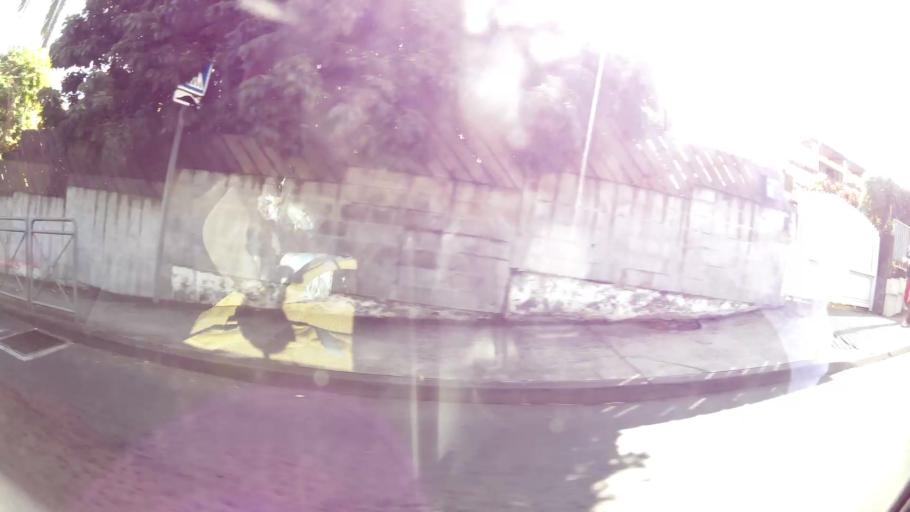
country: RE
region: Reunion
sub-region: Reunion
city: Le Tampon
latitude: -21.2811
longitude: 55.5113
